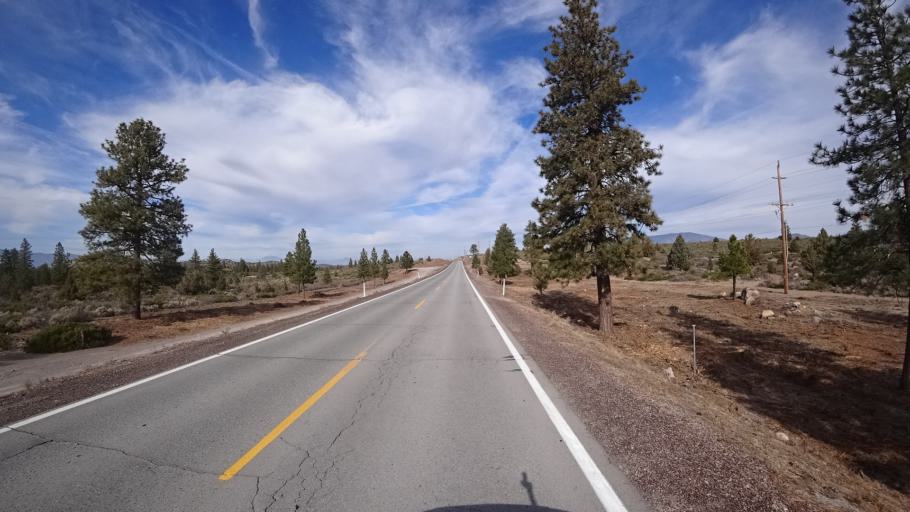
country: US
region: California
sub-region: Siskiyou County
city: Weed
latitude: 41.4885
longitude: -122.3623
